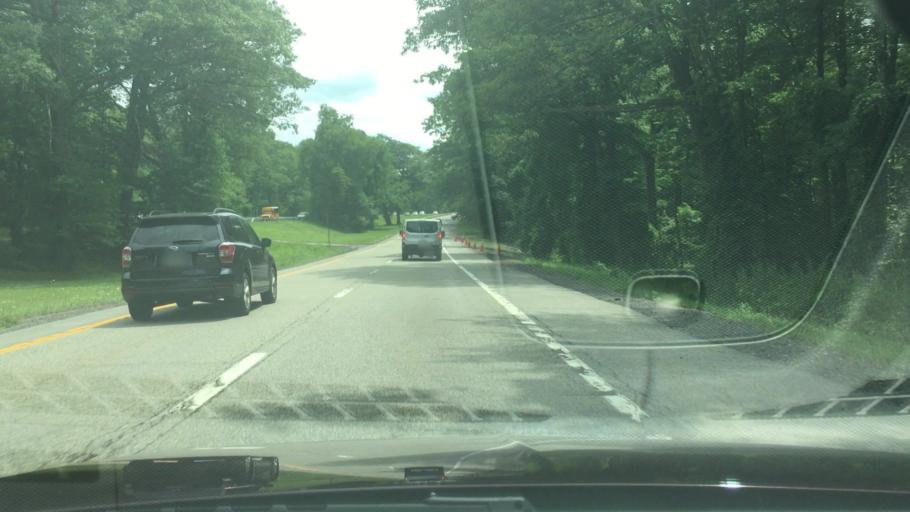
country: US
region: New York
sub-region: Dutchess County
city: Brinckerhoff
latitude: 41.4469
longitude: -73.8162
